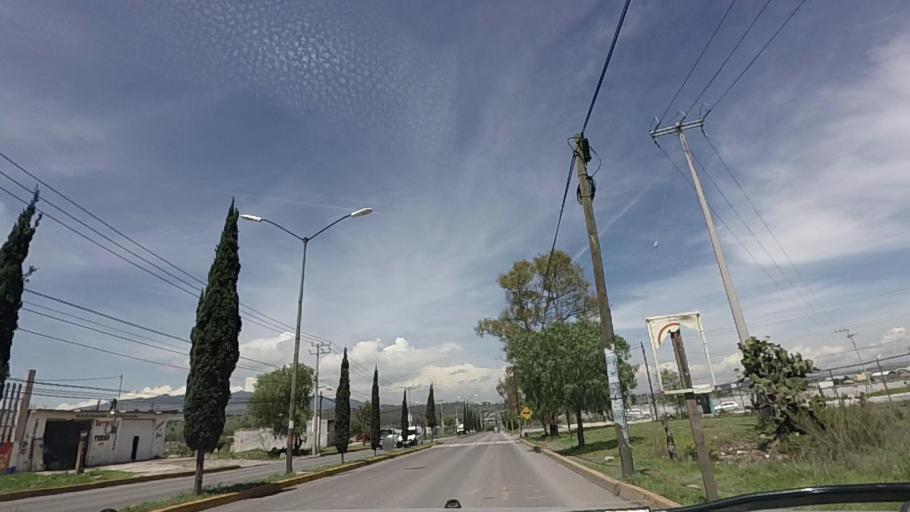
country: MX
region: Mexico
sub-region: Huehuetoca
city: Jorobas
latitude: 19.8271
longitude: -99.2371
